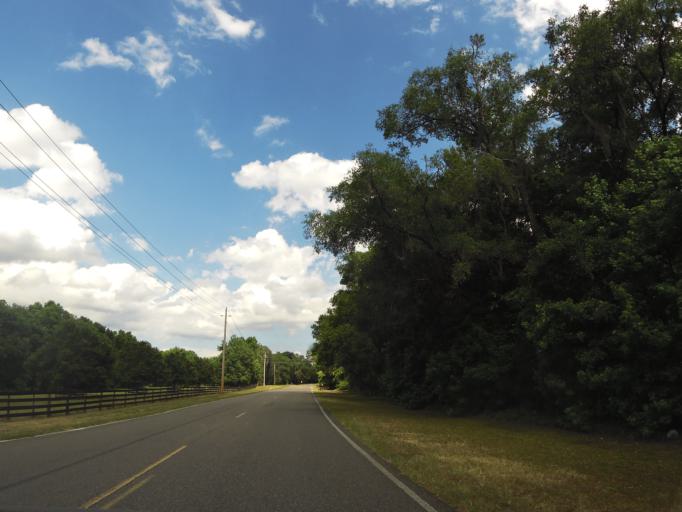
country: US
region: Florida
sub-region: Clay County
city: Keystone Heights
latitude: 29.7936
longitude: -81.9088
